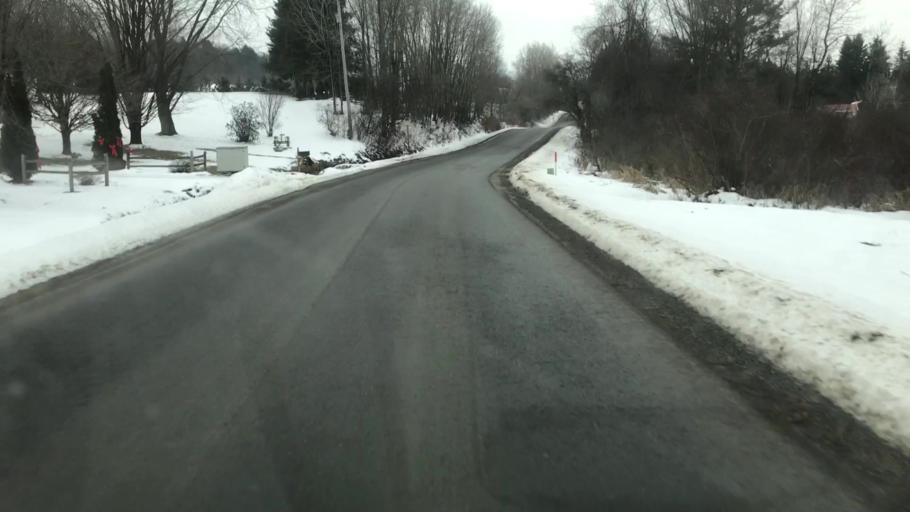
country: US
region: New York
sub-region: Cortland County
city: Cortland West
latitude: 42.6713
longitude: -76.2761
